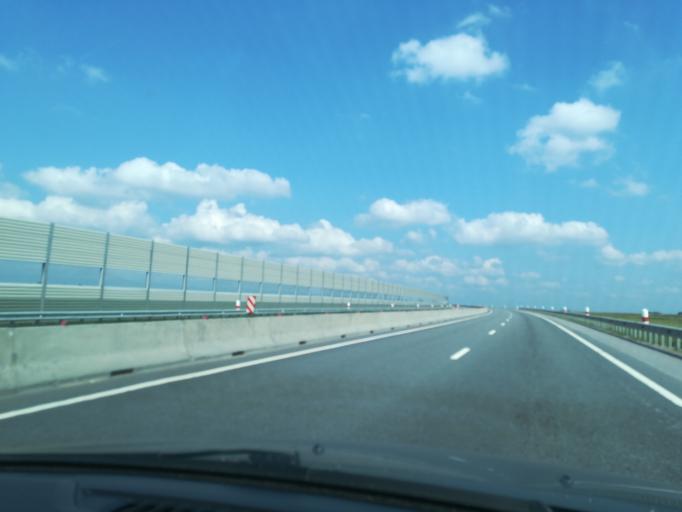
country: RU
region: Leningrad
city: Kingisepp
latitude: 59.5750
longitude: 28.7688
